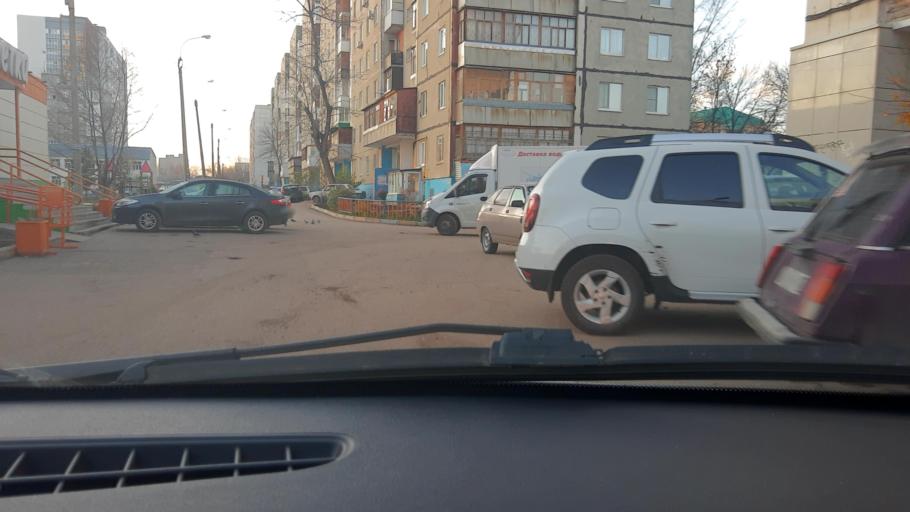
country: RU
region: Bashkortostan
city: Mikhaylovka
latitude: 54.7129
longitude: 55.8270
